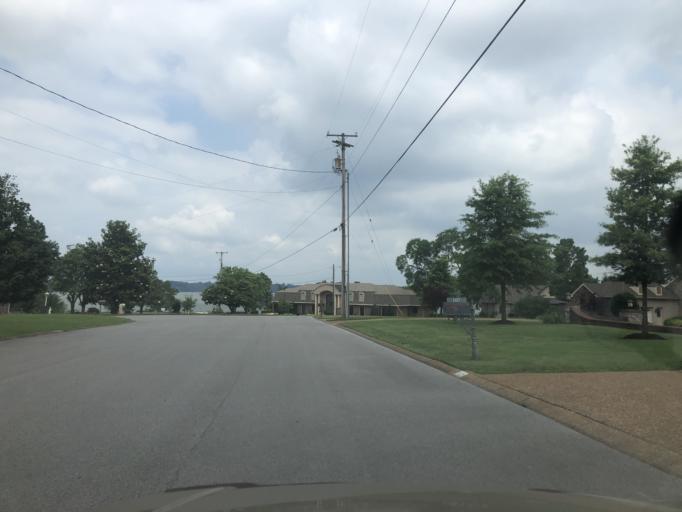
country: US
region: Tennessee
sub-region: Davidson County
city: Lakewood
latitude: 36.2423
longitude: -86.6176
